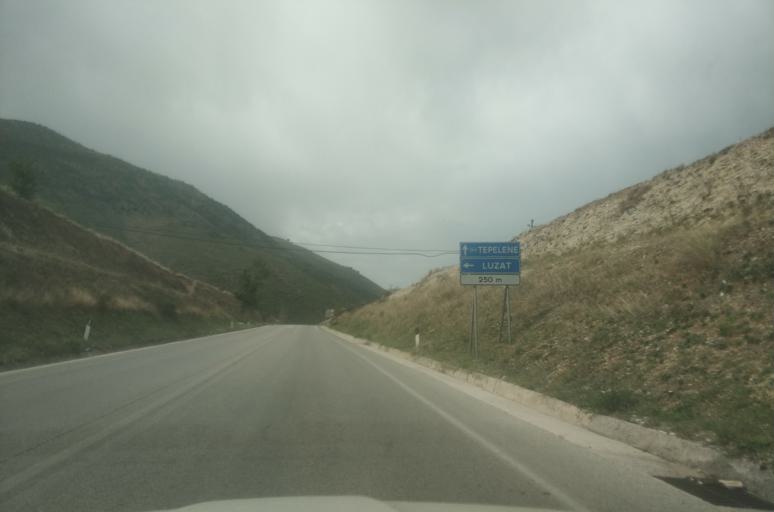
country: AL
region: Gjirokaster
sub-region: Rrethi i Tepelenes
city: Tepelene
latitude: 40.2684
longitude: 20.0471
